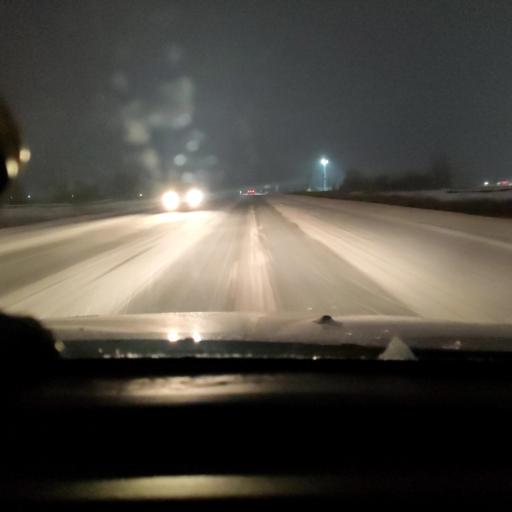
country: RU
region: Samara
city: Otradnyy
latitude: 53.3450
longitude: 51.3008
